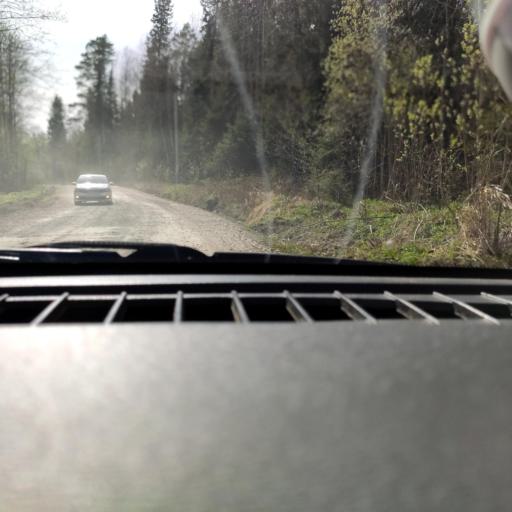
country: RU
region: Perm
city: Kondratovo
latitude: 58.2576
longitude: 56.1011
